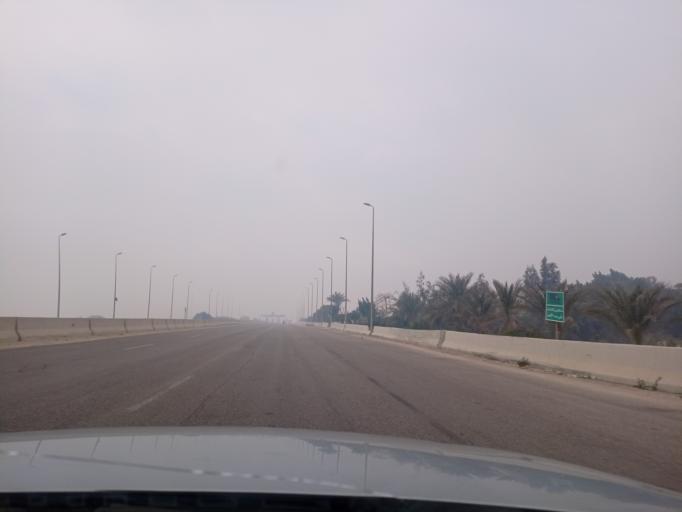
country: EG
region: Al Jizah
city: Al `Ayyat
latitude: 29.6836
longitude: 31.2301
